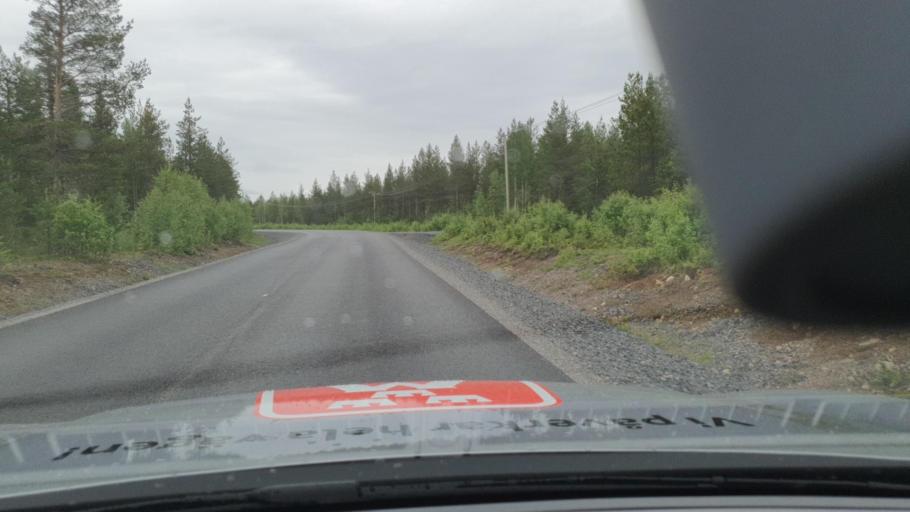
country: SE
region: Norrbotten
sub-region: Overkalix Kommun
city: OEverkalix
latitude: 66.7162
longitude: 23.1925
